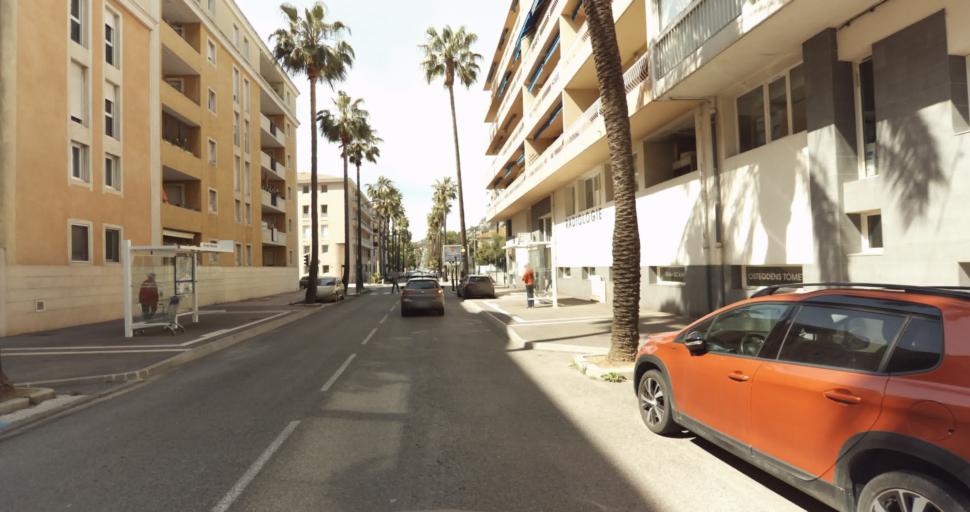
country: FR
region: Provence-Alpes-Cote d'Azur
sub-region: Departement du Var
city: Hyeres
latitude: 43.1110
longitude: 6.1241
